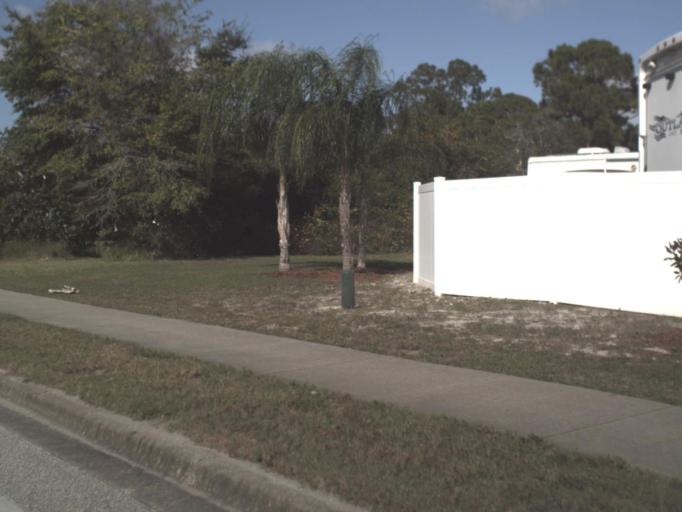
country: US
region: Florida
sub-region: Volusia County
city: Port Orange
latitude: 29.1334
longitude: -81.0291
